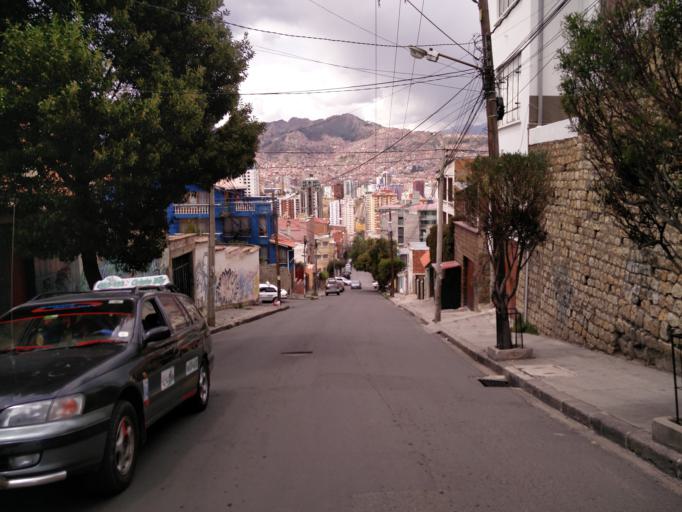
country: BO
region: La Paz
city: La Paz
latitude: -16.5133
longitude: -68.1319
